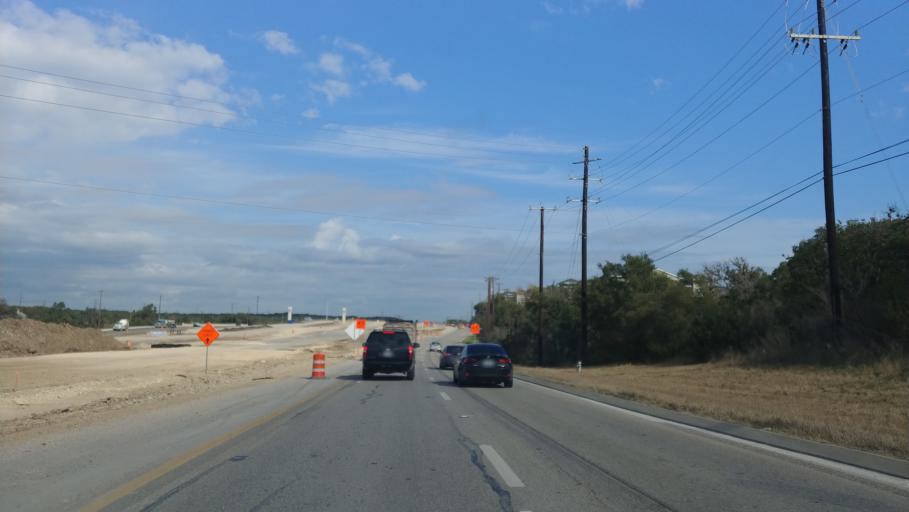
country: US
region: Texas
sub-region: Bexar County
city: Leon Valley
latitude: 29.4595
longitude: -98.7111
